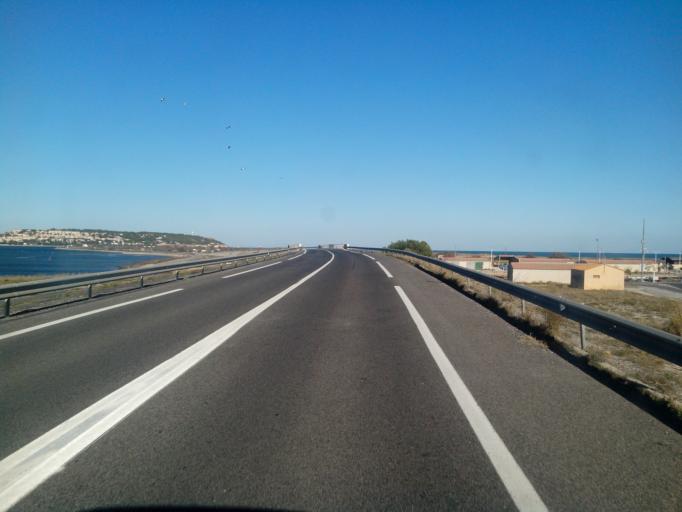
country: FR
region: Languedoc-Roussillon
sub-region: Departement de l'Aude
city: Leucate
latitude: 42.8849
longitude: 3.0469
